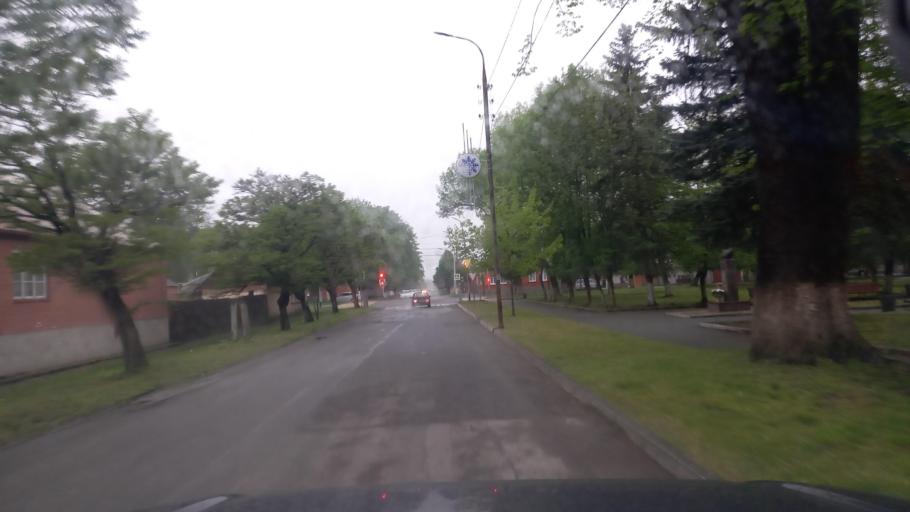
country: RU
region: North Ossetia
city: Alagir
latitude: 43.0392
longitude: 44.2210
